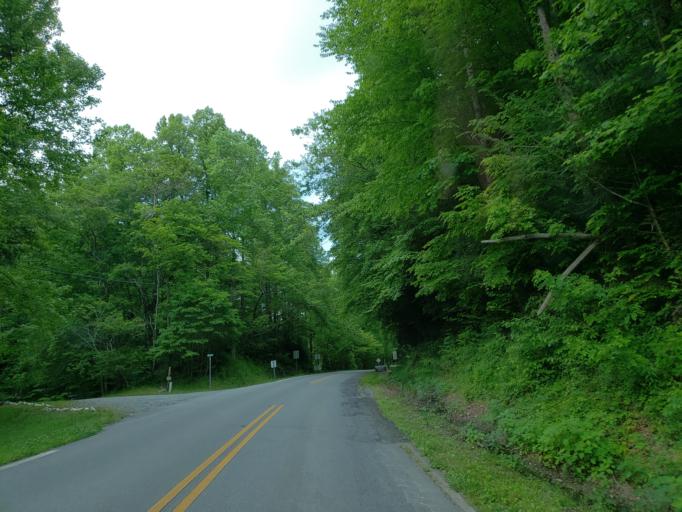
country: US
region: Georgia
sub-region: Fannin County
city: Blue Ridge
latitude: 34.8405
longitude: -84.3983
